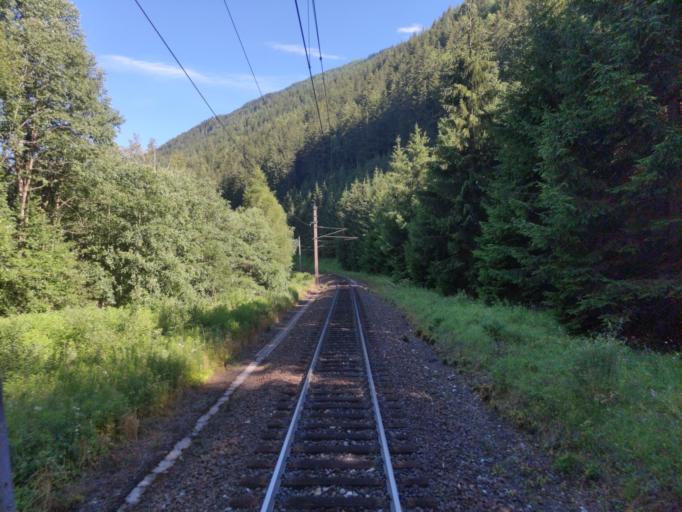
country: AT
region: Tyrol
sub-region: Politischer Bezirk Landeck
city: Strengen
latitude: 47.1318
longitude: 10.4270
